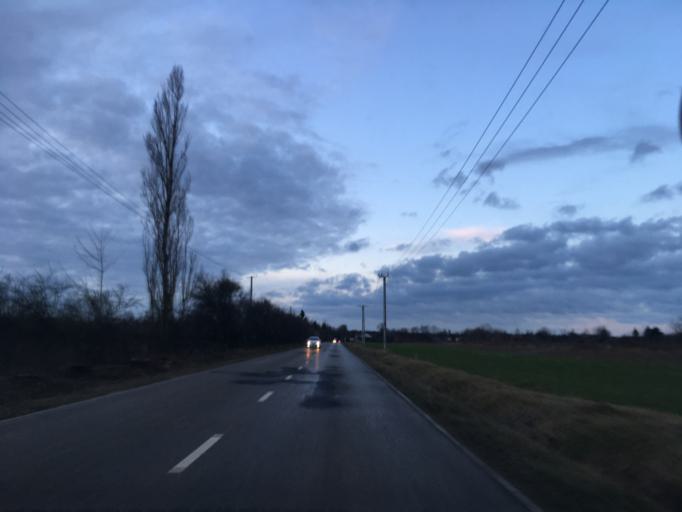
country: PL
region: Masovian Voivodeship
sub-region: Powiat pruszkowski
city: Owczarnia
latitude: 52.0789
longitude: 20.7057
